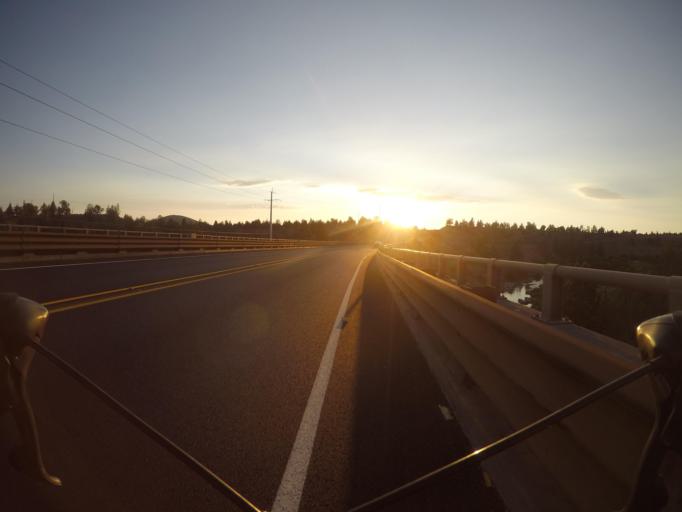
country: US
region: Oregon
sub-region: Deschutes County
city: Redmond
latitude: 44.2734
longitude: -121.2579
